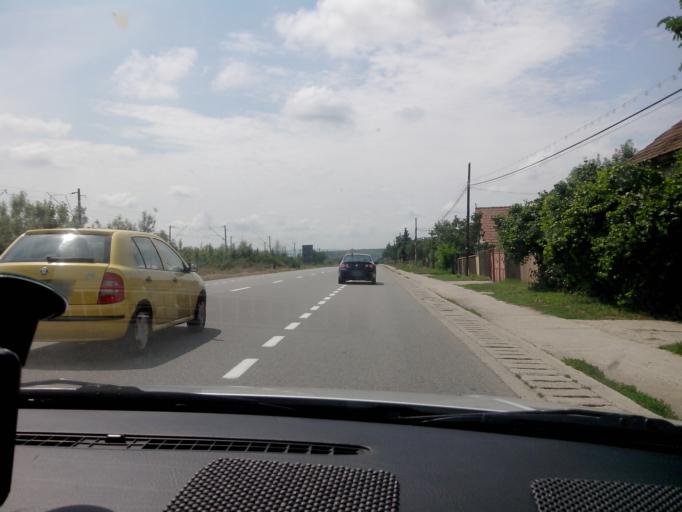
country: RO
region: Cluj
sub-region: Comuna Apahida
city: Apahida
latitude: 46.8540
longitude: 23.7576
